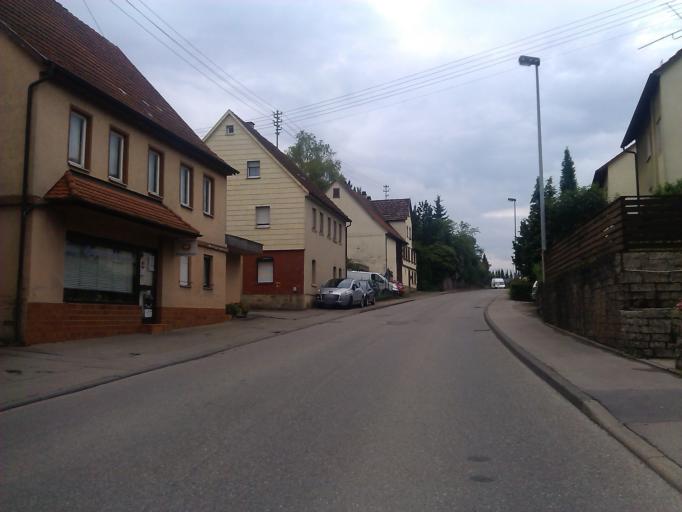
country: DE
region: Baden-Wuerttemberg
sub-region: Regierungsbezirk Stuttgart
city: Oberrot
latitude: 49.0036
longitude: 9.6794
